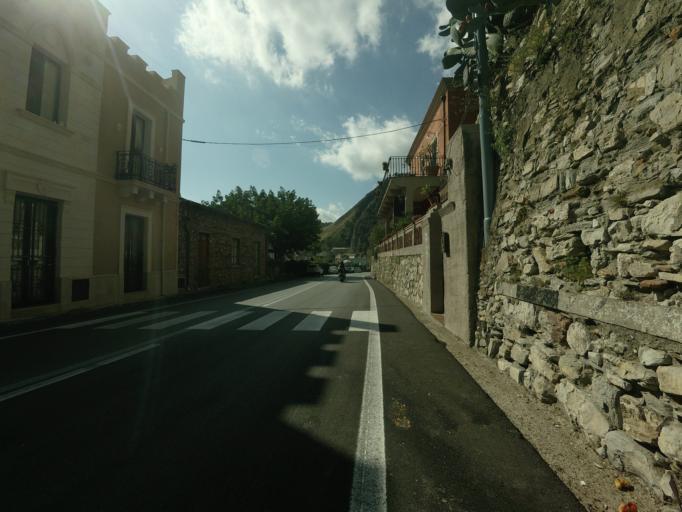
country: IT
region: Sicily
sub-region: Messina
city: Taormina
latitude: 37.8485
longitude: 15.2887
